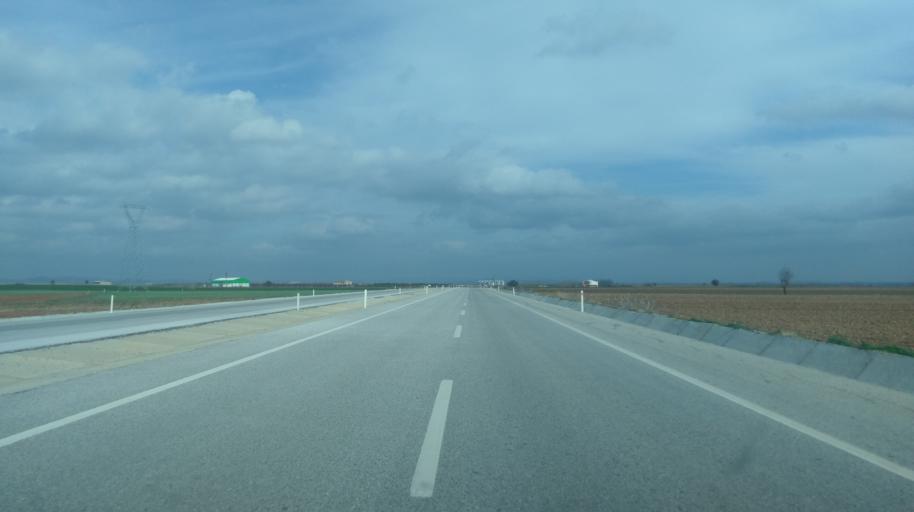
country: TR
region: Kirklareli
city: Inece
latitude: 41.6938
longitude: 27.1386
